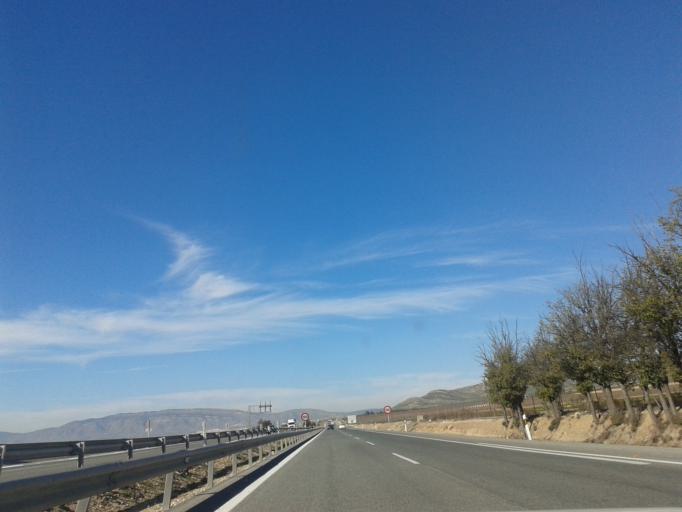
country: ES
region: Valencia
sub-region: Provincia de Alicante
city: Villena
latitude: 38.6740
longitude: -0.8901
